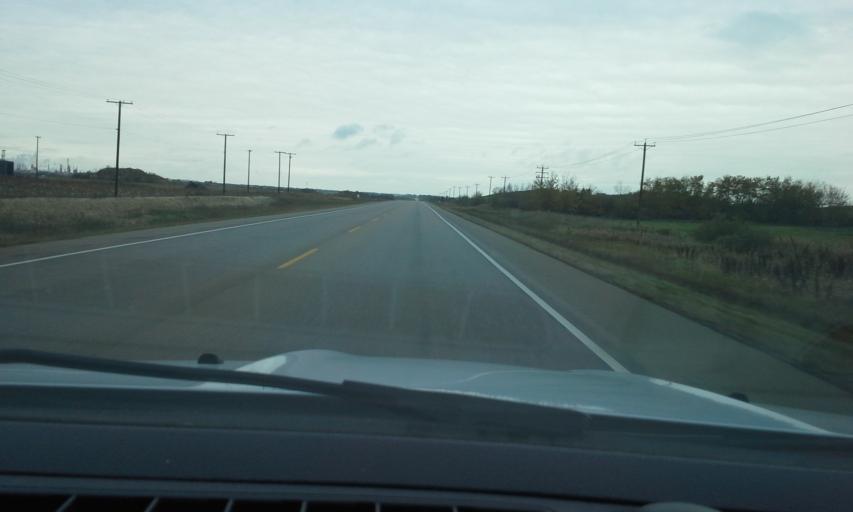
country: CA
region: Saskatchewan
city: Lloydminster
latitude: 53.2780
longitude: -109.8901
